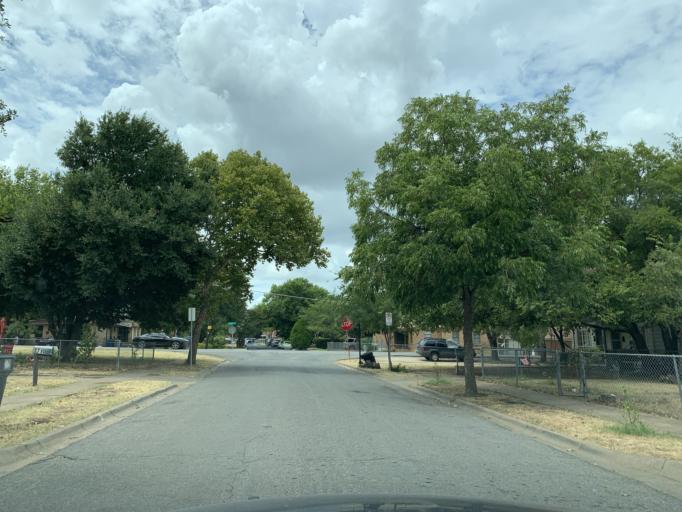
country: US
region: Texas
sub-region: Dallas County
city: Cockrell Hill
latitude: 32.7435
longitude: -96.8801
